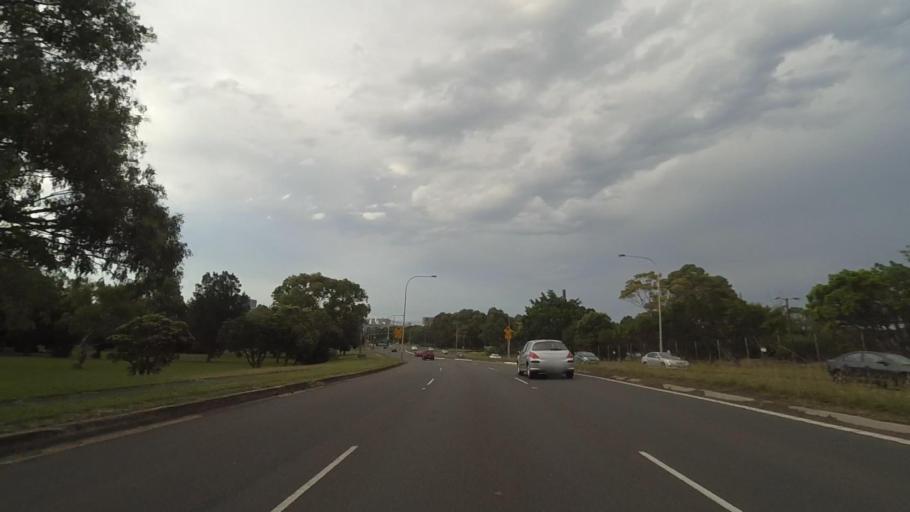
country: AU
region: New South Wales
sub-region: Wollongong
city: Cringila
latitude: -34.4758
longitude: 150.8875
